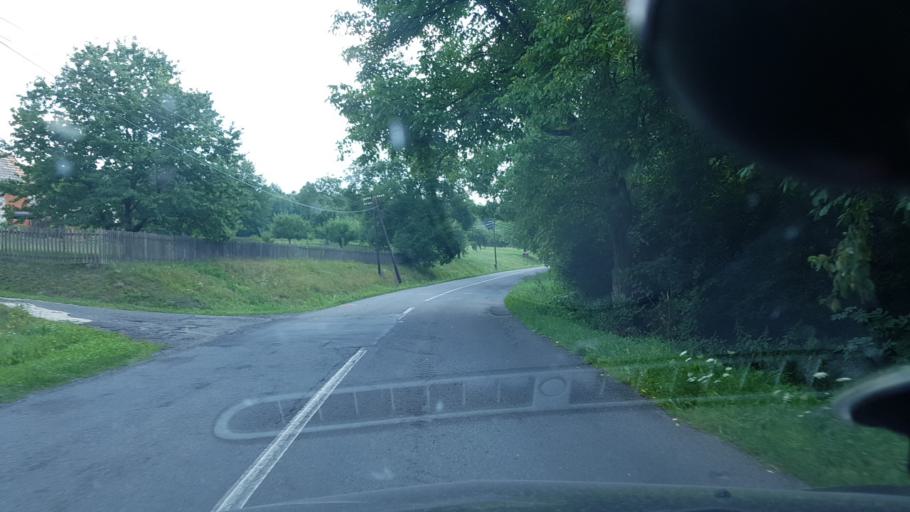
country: SK
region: Banskobystricky
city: Detva
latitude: 48.5062
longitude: 19.3152
